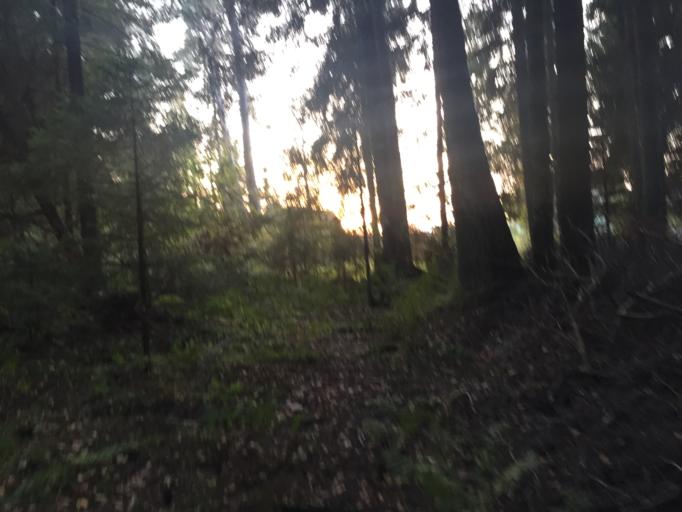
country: LV
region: Salaspils
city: Salaspils
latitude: 56.9182
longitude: 24.4361
